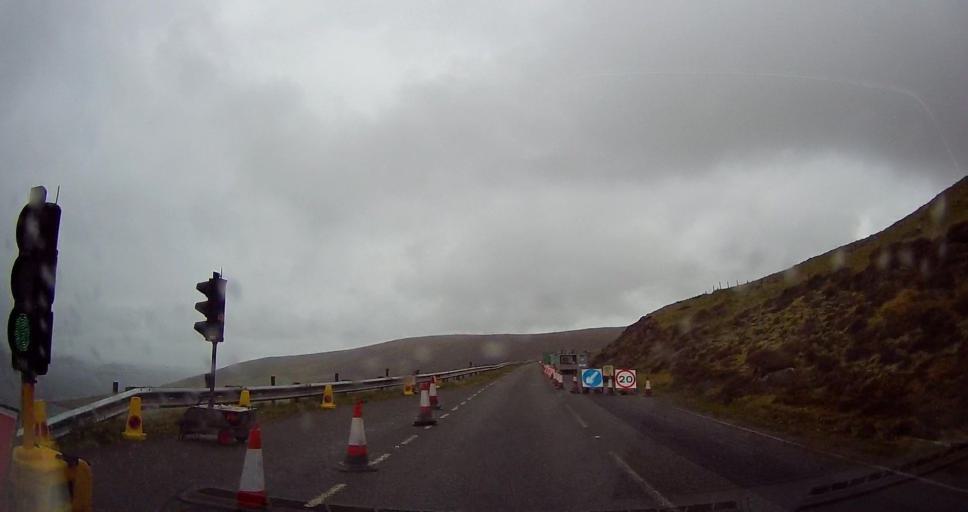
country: GB
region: Scotland
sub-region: Shetland Islands
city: Lerwick
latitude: 60.2377
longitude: -1.3125
